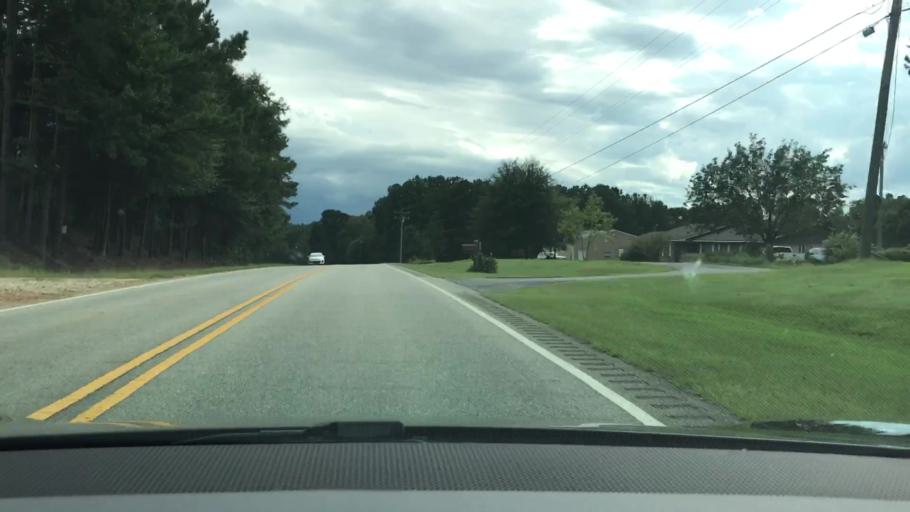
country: US
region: Alabama
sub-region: Coffee County
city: Elba
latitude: 31.5492
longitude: -86.0183
